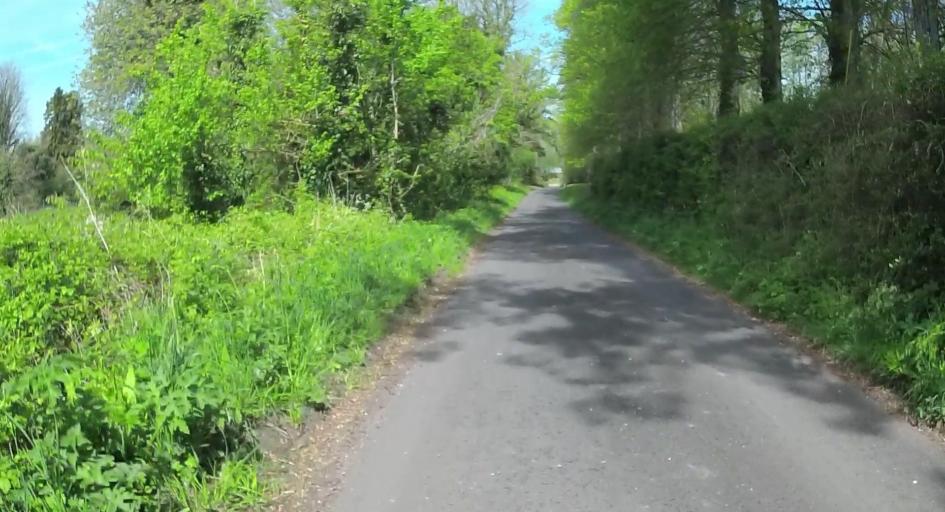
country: GB
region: England
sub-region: Hampshire
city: Abbotts Ann
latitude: 51.1030
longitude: -1.4935
